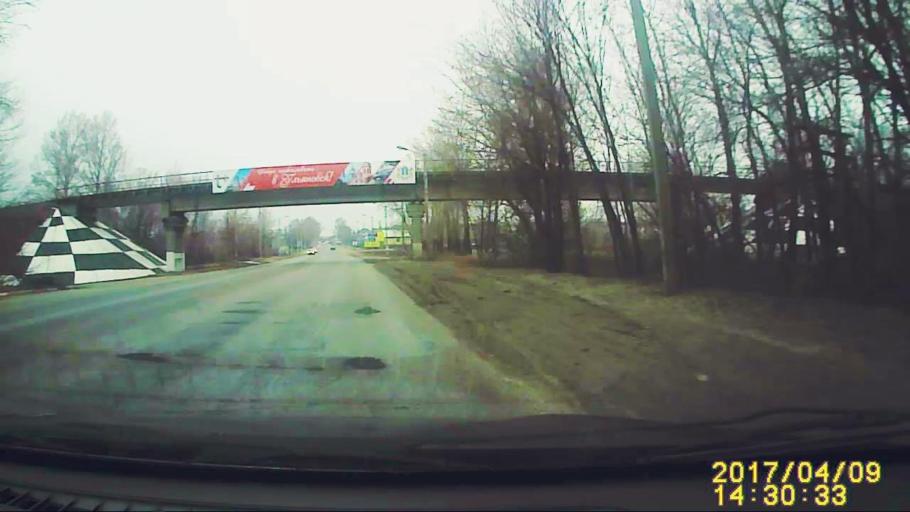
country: RU
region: Ulyanovsk
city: Novoul'yanovsk
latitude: 54.2143
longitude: 48.2977
